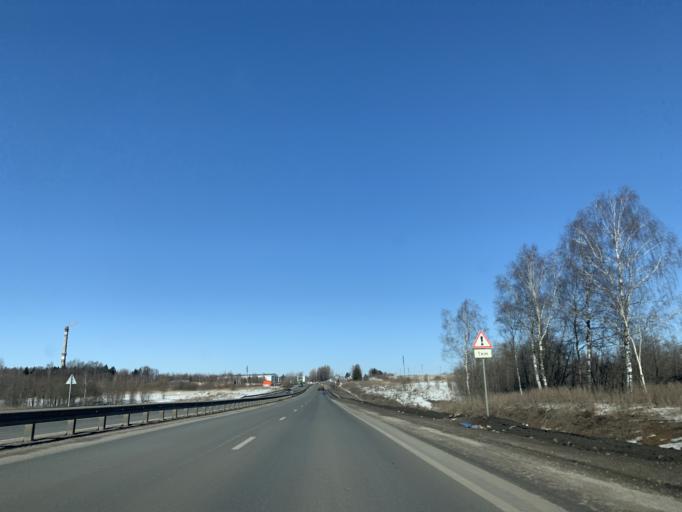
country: RU
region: Jaroslavl
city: Konstantinovskiy
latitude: 57.8406
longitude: 39.5526
